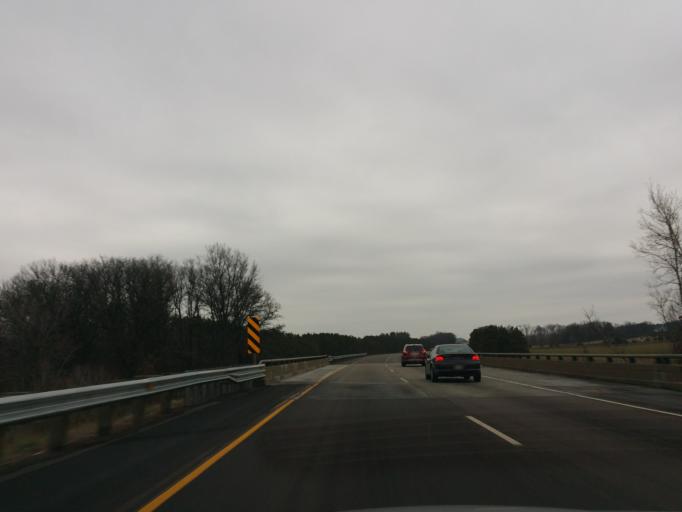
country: US
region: Wisconsin
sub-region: Trempealeau County
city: Osseo
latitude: 44.5470
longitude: -91.1635
